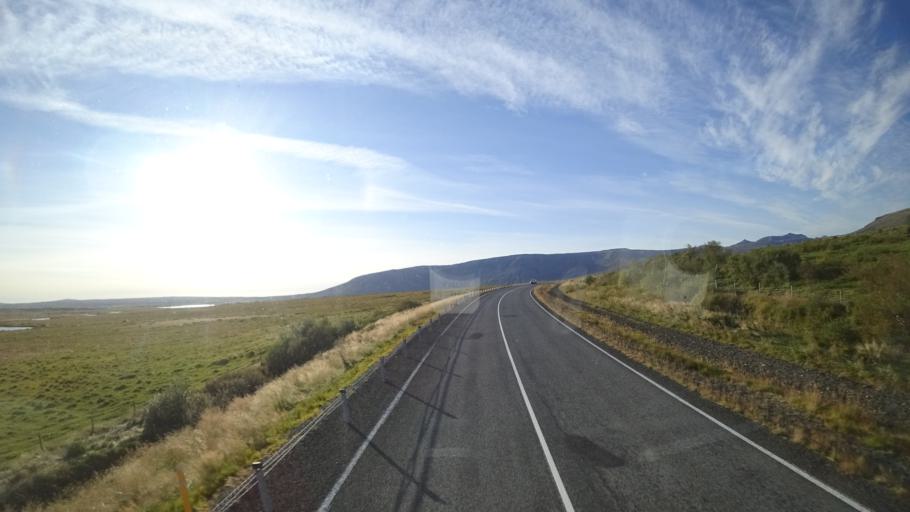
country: IS
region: South
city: Selfoss
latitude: 64.2246
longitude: -20.6281
